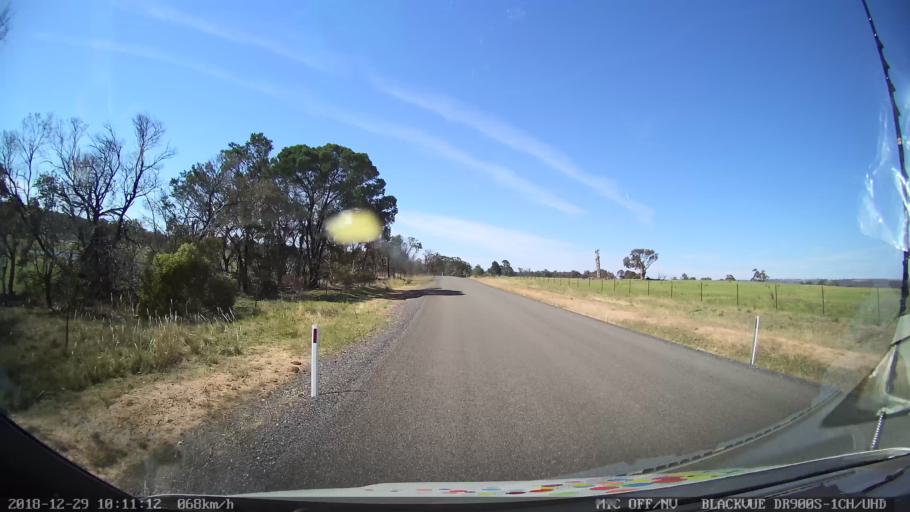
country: AU
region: New South Wales
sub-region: Yass Valley
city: Gundaroo
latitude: -34.8812
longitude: 149.4524
